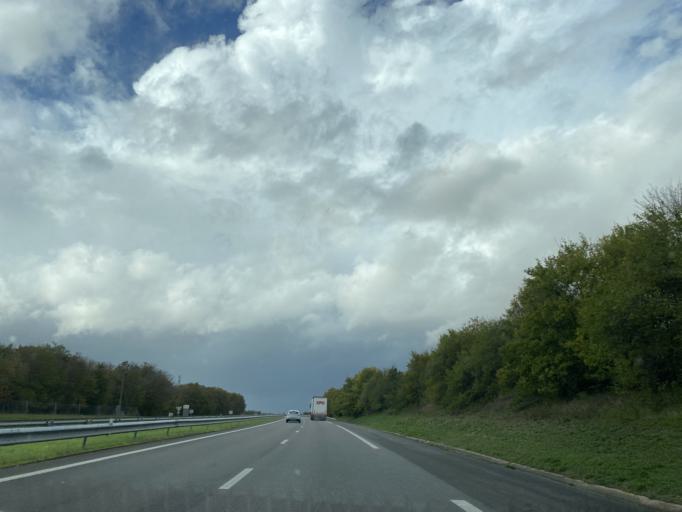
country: FR
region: Centre
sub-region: Departement du Cher
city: Plaimpied-Givaudins
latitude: 46.9800
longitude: 2.4204
